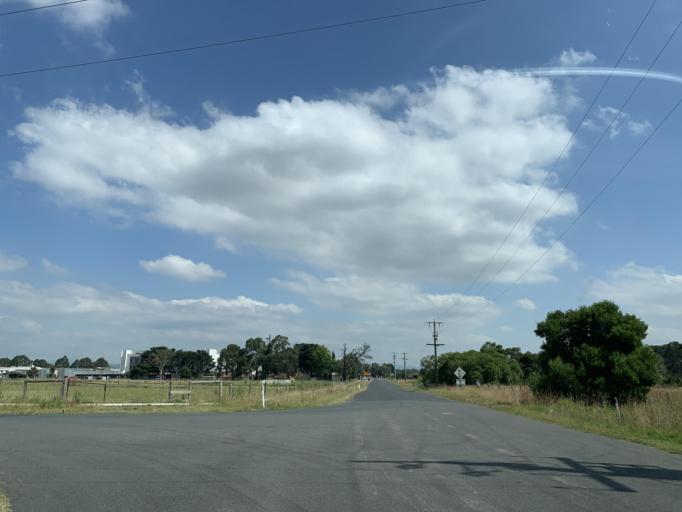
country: AU
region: Victoria
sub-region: Latrobe
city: Traralgon
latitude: -38.2146
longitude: 146.4694
